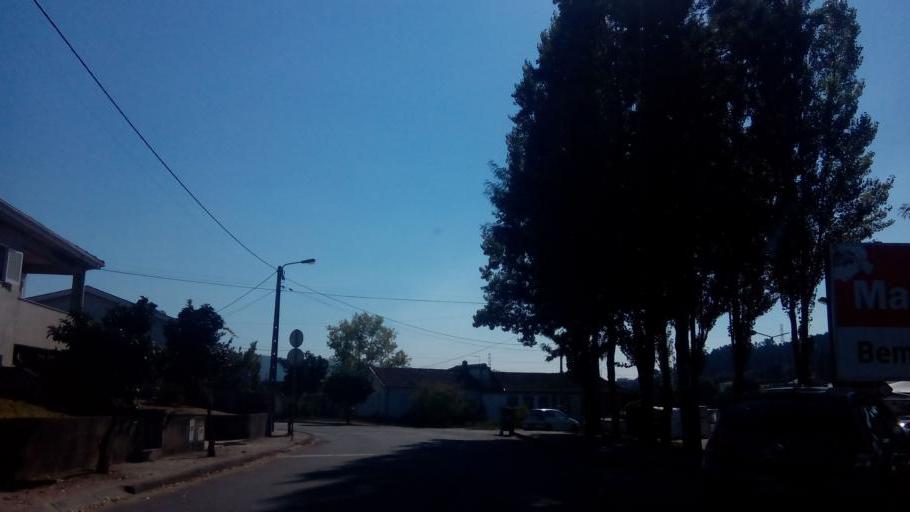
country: PT
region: Porto
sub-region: Paredes
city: Casteloes de Cepeda
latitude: 41.1973
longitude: -8.3351
